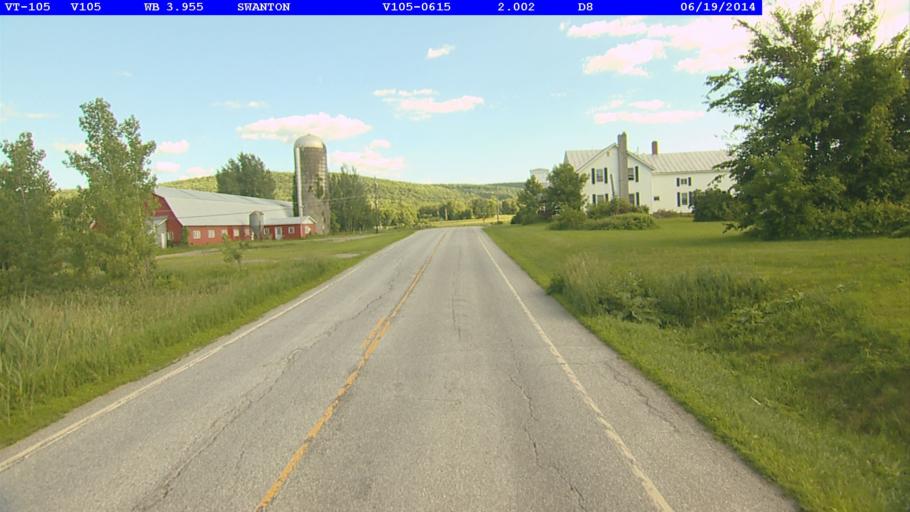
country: US
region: Vermont
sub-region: Franklin County
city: Saint Albans
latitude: 44.8612
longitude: -73.0326
